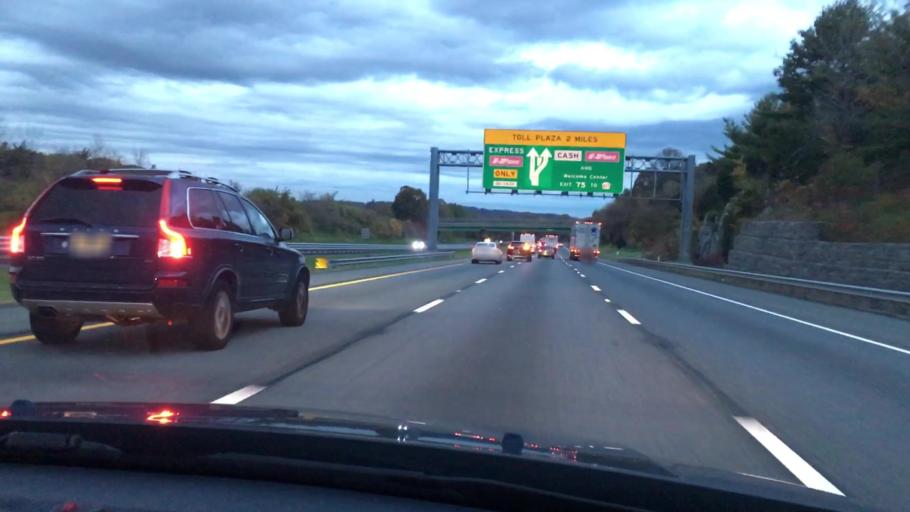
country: US
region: New Jersey
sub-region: Warren County
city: Alpha
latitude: 40.6629
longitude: -75.1734
